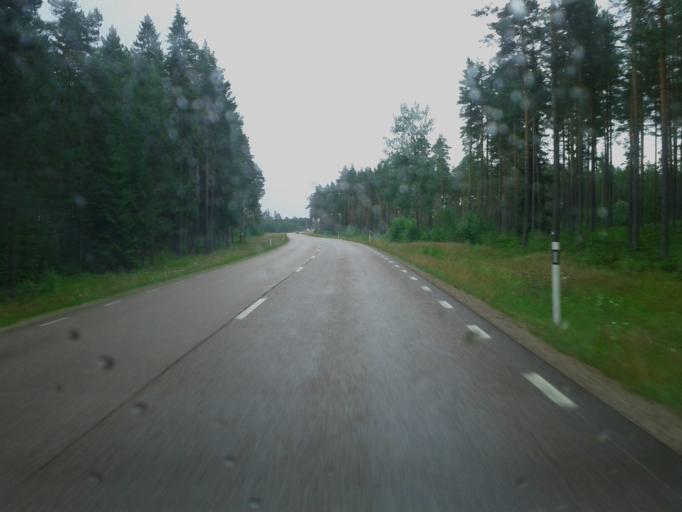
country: SE
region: Dalarna
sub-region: Mora Kommun
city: Mora
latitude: 60.9824
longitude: 14.6886
